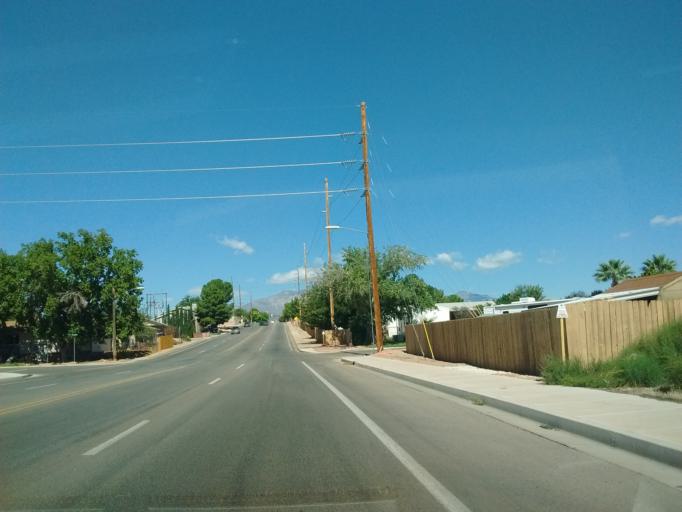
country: US
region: Utah
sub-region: Washington County
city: Washington
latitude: 37.1273
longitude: -113.5049
